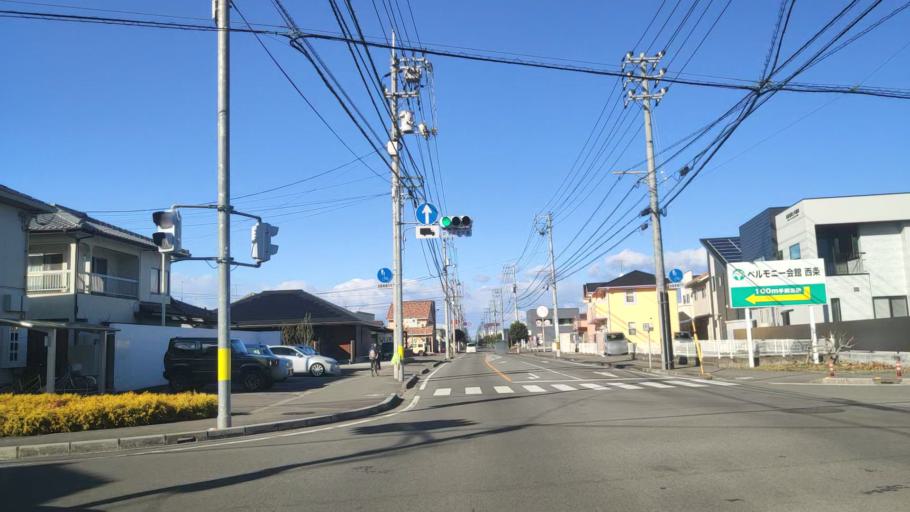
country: JP
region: Ehime
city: Saijo
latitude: 33.9214
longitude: 133.1918
